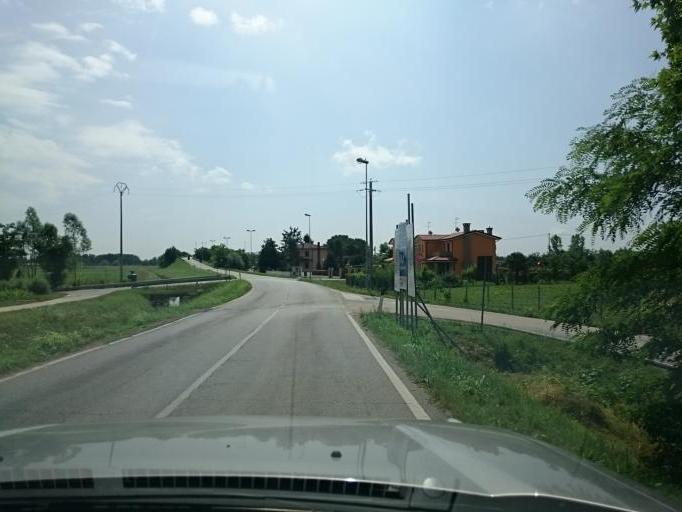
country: IT
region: Veneto
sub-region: Provincia di Padova
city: Masera di Padova
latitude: 45.3404
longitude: 11.8480
